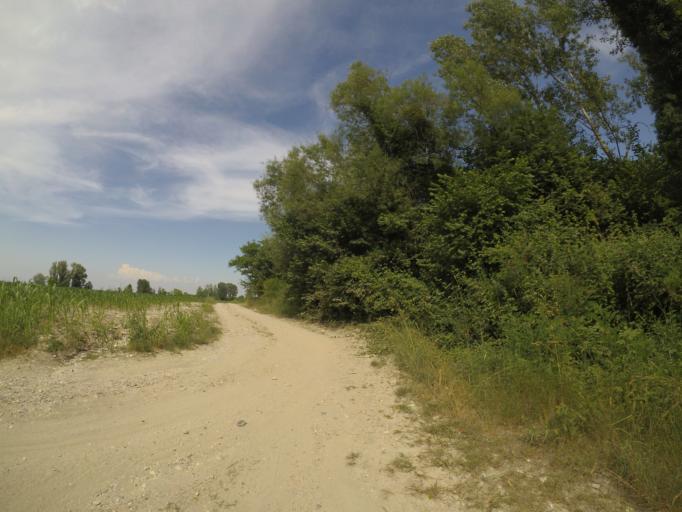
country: IT
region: Friuli Venezia Giulia
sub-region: Provincia di Udine
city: Camino al Tagliamento
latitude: 45.9113
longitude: 12.9232
